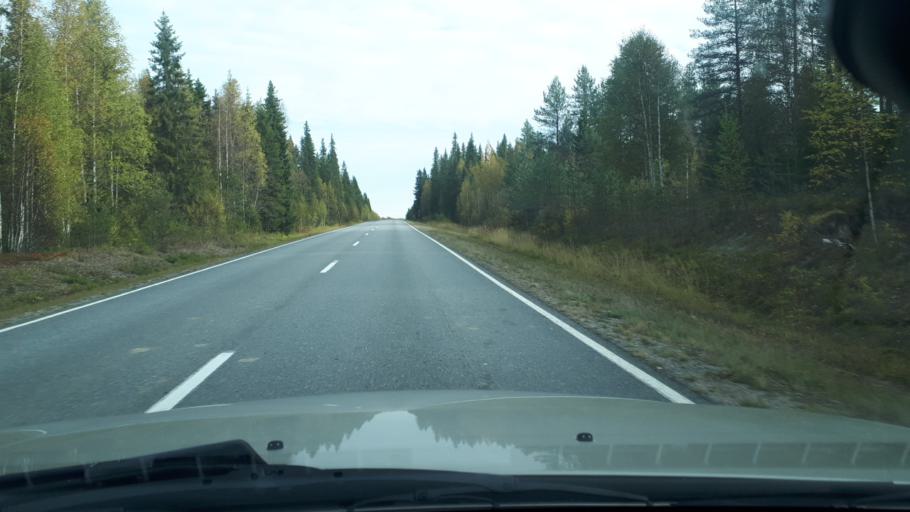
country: FI
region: Lapland
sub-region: Rovaniemi
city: Ranua
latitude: 65.9740
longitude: 26.1109
